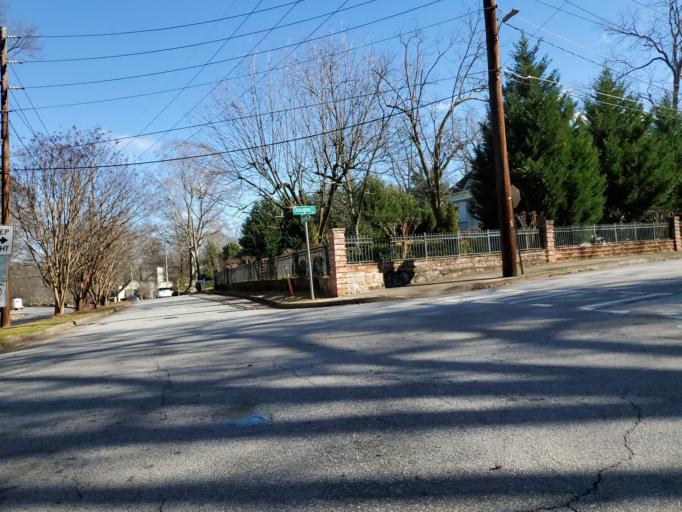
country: US
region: Georgia
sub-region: DeKalb County
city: Decatur
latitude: 33.7494
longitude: -84.3197
